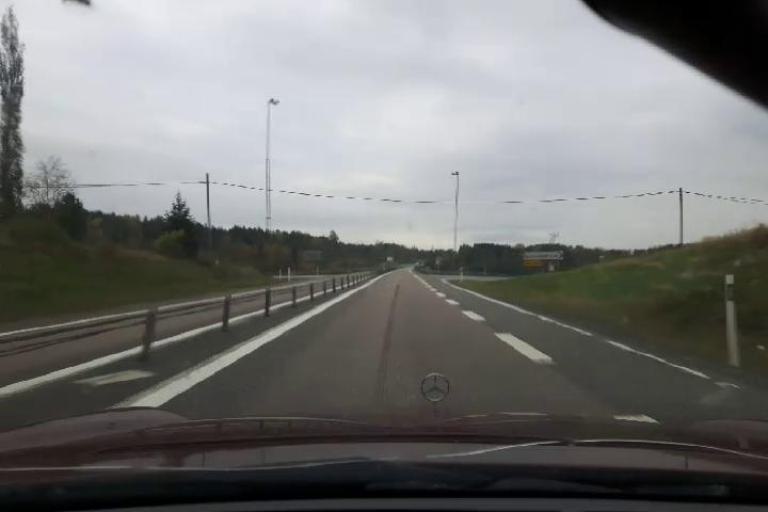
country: SE
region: Vaesternorrland
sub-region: Kramfors Kommun
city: Nordingra
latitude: 62.9227
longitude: 18.0994
